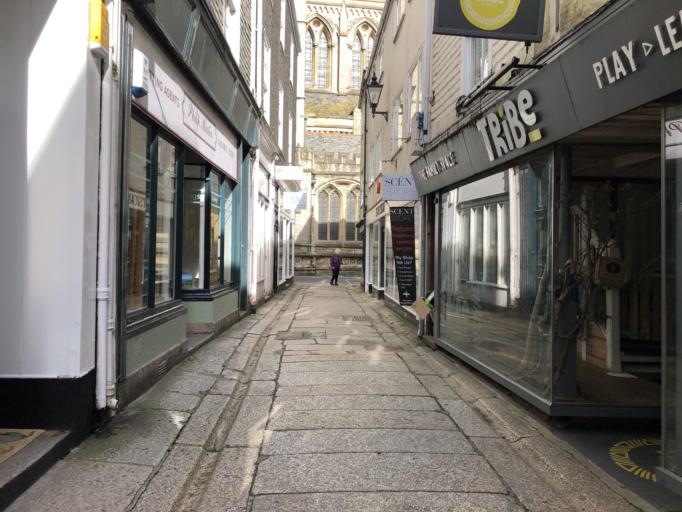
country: GB
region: England
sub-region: Cornwall
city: Truro
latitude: 50.2635
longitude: -5.0510
